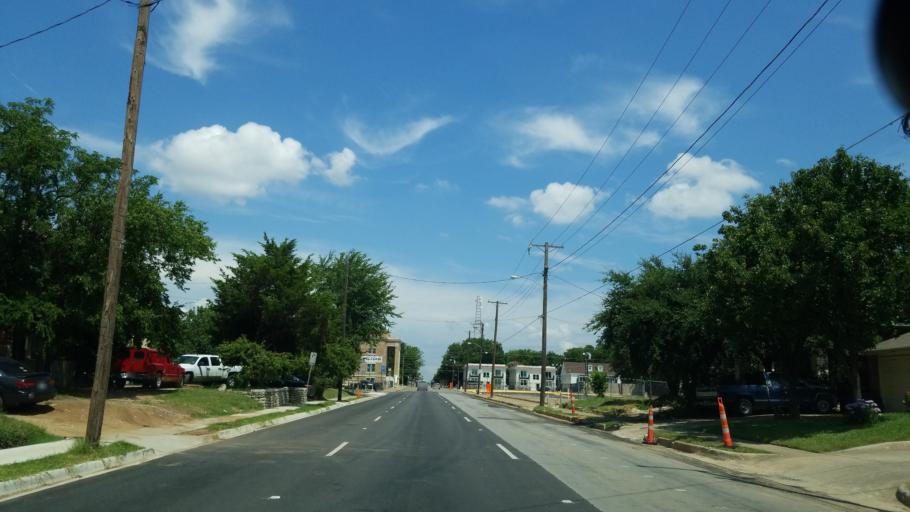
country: US
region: Texas
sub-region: Dallas County
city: Dallas
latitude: 32.7928
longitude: -96.7723
